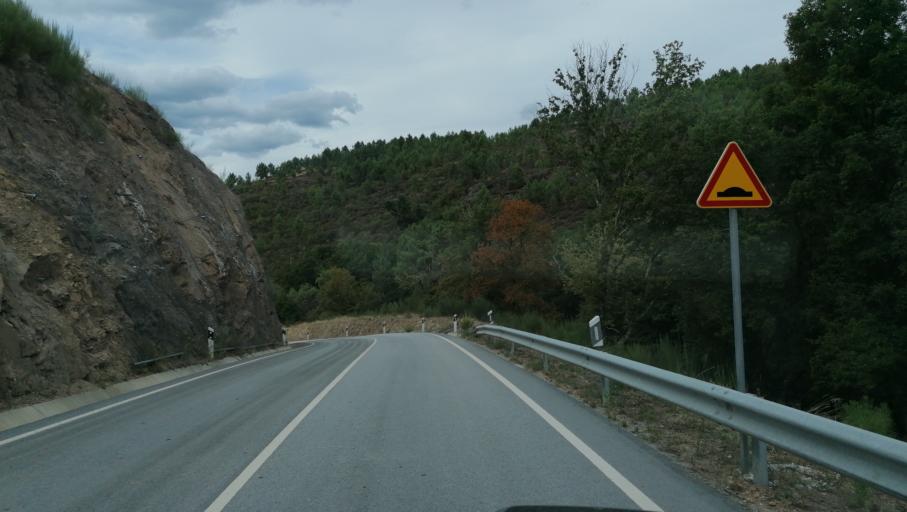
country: PT
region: Vila Real
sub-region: Vila Pouca de Aguiar
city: Vila Pouca de Aguiar
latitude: 41.5646
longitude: -7.7148
